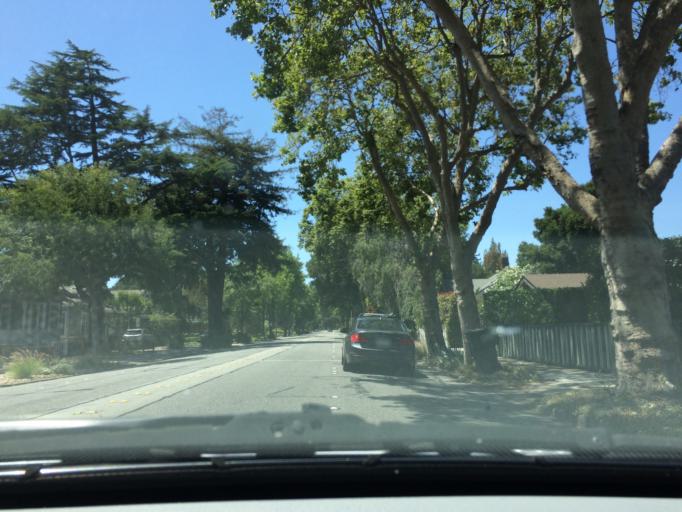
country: US
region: California
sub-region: Santa Clara County
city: Palo Alto
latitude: 37.4517
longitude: -122.1582
